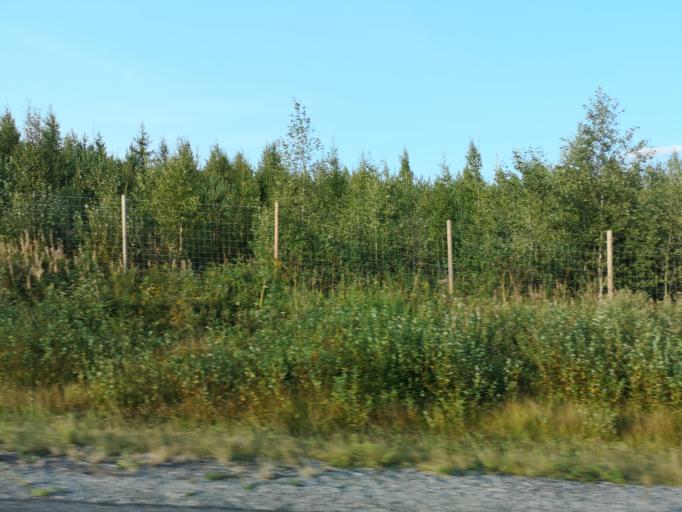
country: FI
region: Paijanne Tavastia
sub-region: Lahti
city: Hartola
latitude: 61.4232
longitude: 26.0217
